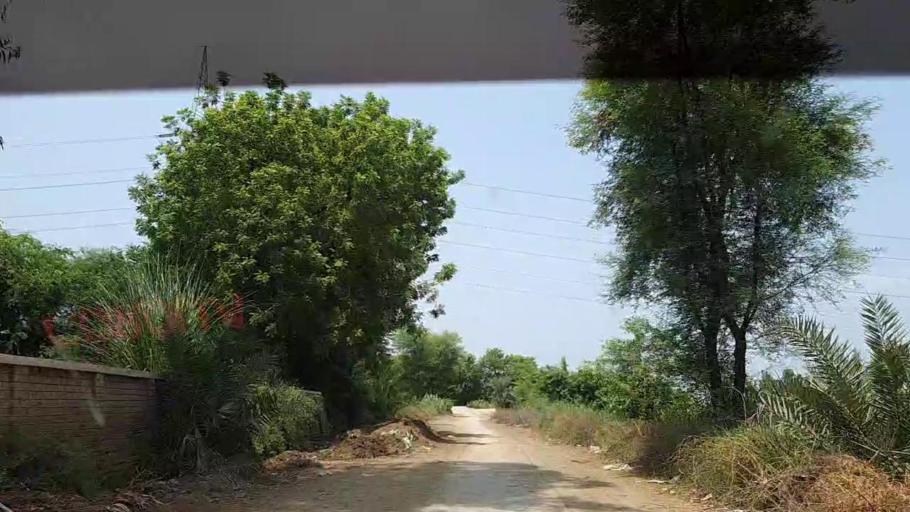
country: PK
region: Sindh
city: Adilpur
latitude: 27.8795
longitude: 69.2624
